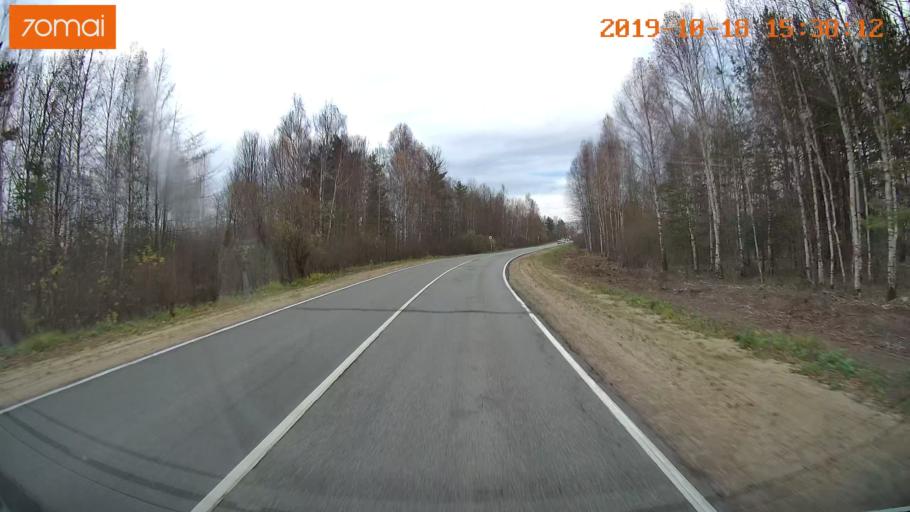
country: RU
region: Vladimir
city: Golovino
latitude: 55.9079
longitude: 40.6090
